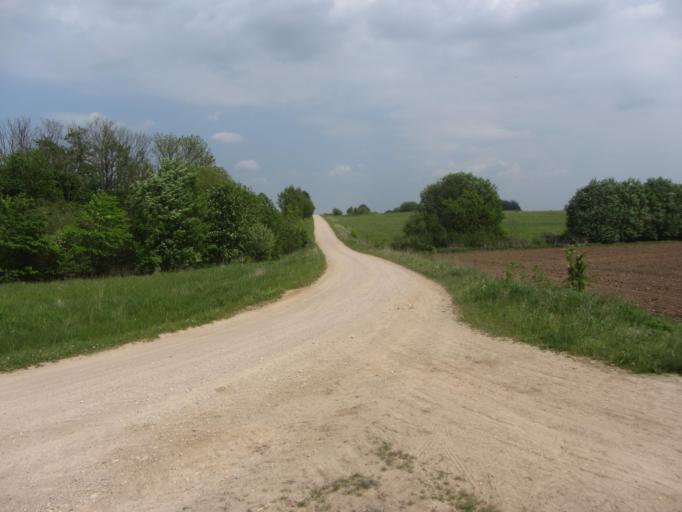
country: LT
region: Utenos apskritis
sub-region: Utena
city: Utena
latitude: 55.5562
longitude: 25.3848
